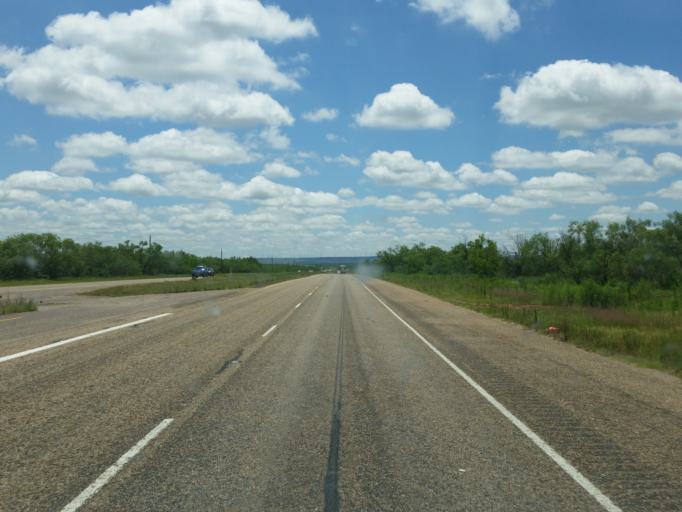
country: US
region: Texas
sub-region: Garza County
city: Post
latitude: 33.0530
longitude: -101.2113
